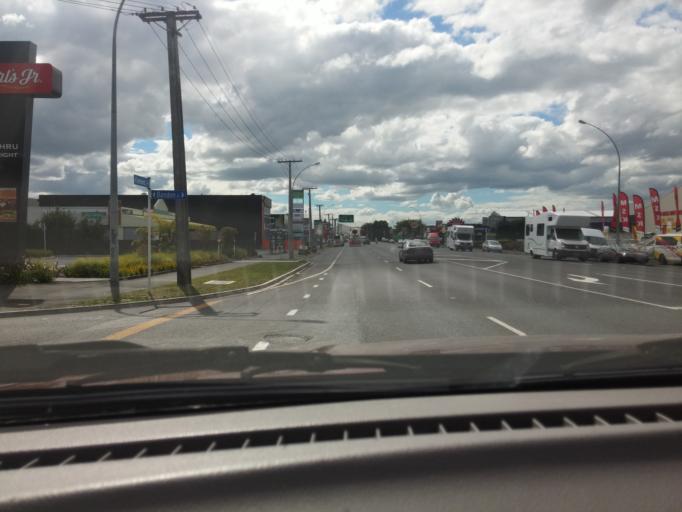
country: NZ
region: Waikato
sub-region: Hamilton City
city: Hamilton
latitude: -37.7919
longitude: 175.2601
